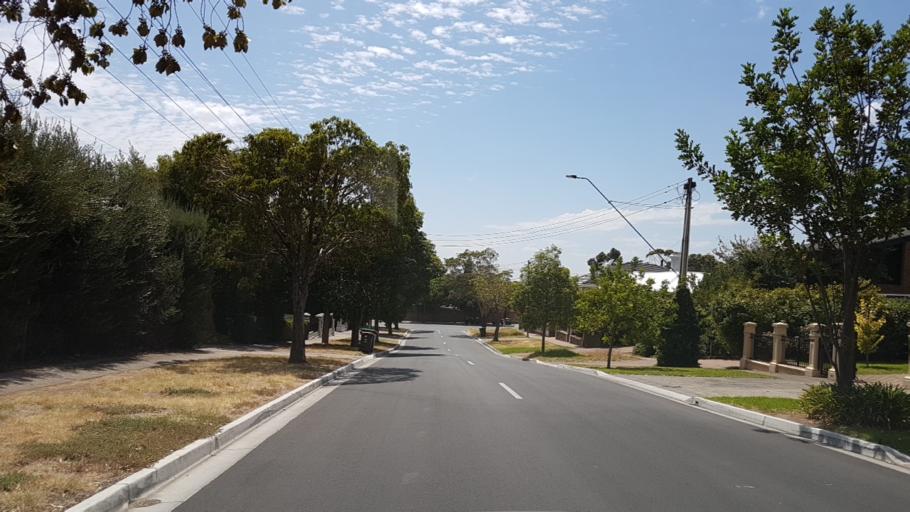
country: AU
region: South Australia
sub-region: Burnside
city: Hazelwood Park
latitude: -34.9390
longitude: 138.6657
